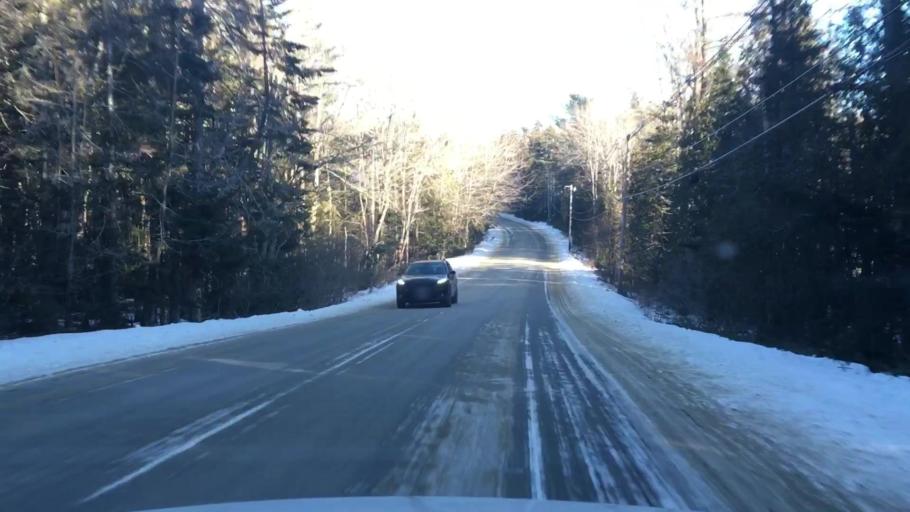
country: US
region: Maine
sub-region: Hancock County
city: Castine
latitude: 44.3598
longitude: -68.7546
